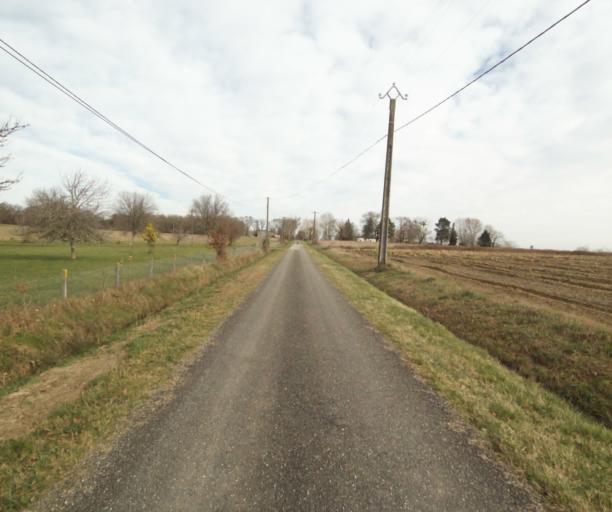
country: FR
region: Aquitaine
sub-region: Departement des Landes
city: Gabarret
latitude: 43.9822
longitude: -0.0061
